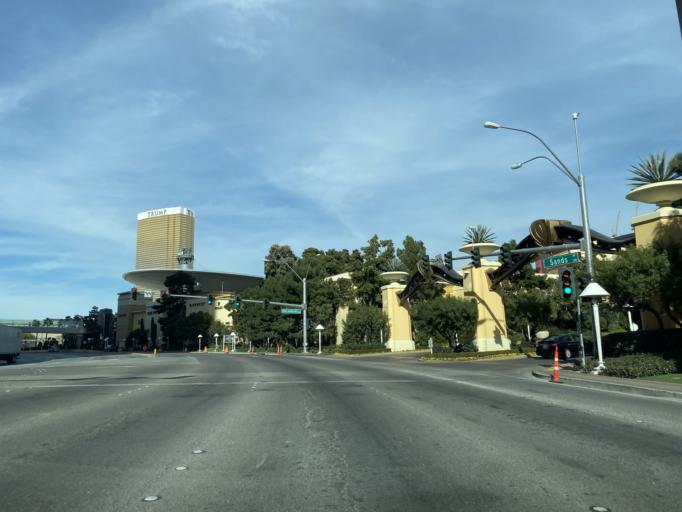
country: US
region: Nevada
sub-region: Clark County
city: Paradise
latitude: 36.1244
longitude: -115.1667
